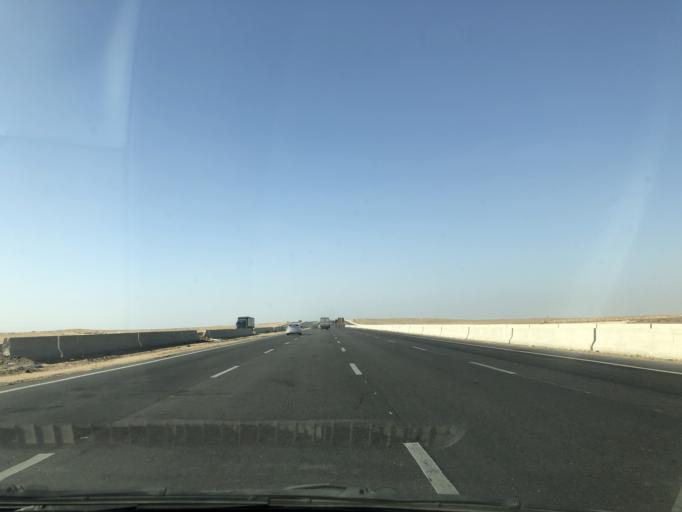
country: EG
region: Al Jizah
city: Madinat Sittah Uktubar
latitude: 30.0165
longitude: 30.8460
